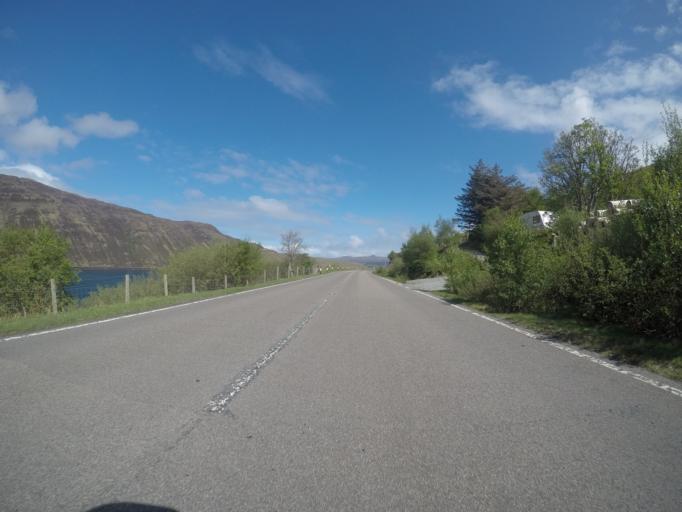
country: GB
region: Scotland
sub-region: Highland
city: Portree
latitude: 57.3076
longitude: -6.1299
